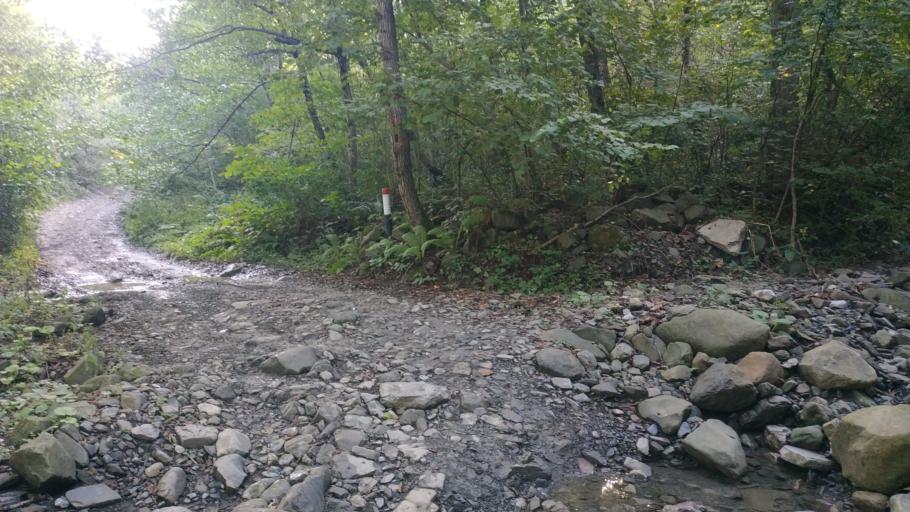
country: RU
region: Krasnodarskiy
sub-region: Sochi City
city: Lazarevskoye
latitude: 43.9916
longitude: 39.3852
